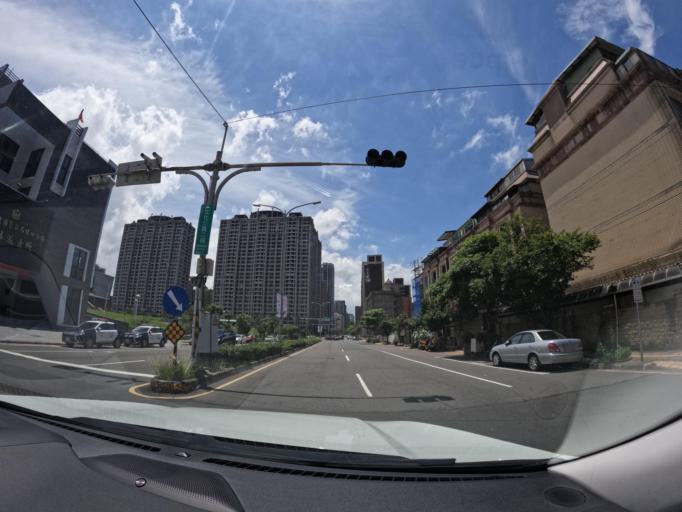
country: TW
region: Taipei
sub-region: Taipei
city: Banqiao
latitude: 25.0877
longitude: 121.3797
